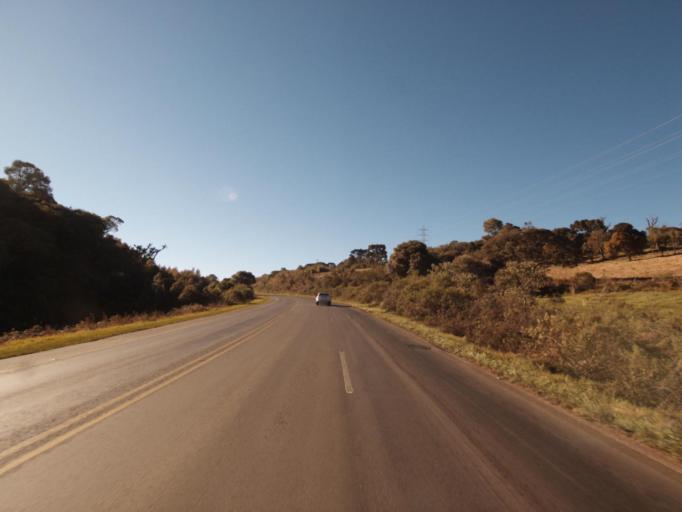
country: BR
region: Santa Catarina
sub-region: Concordia
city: Concordia
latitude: -26.8883
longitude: -51.9965
